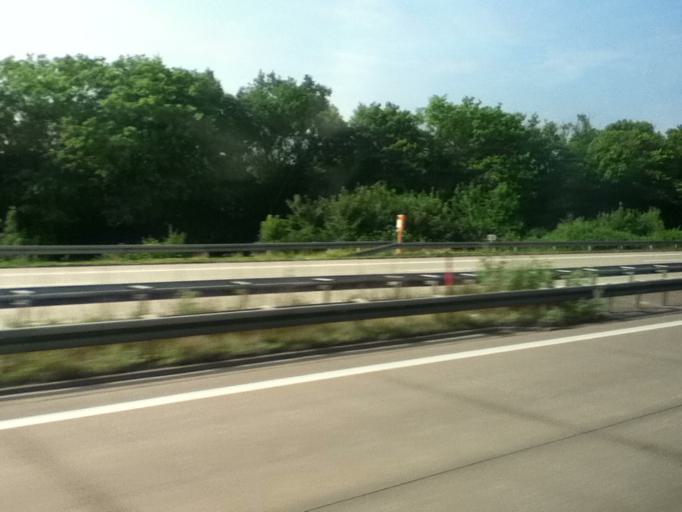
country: DE
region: Saxony
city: Reinsberg
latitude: 51.0601
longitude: 13.4056
